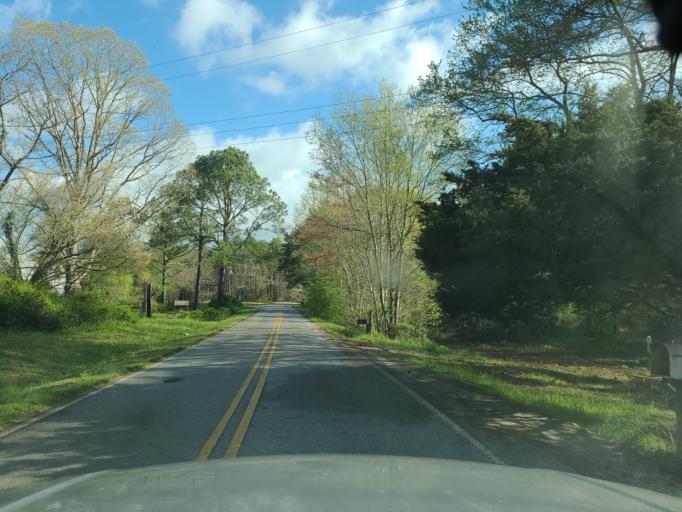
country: US
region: North Carolina
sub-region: Rutherford County
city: Forest City
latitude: 35.4143
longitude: -81.8168
